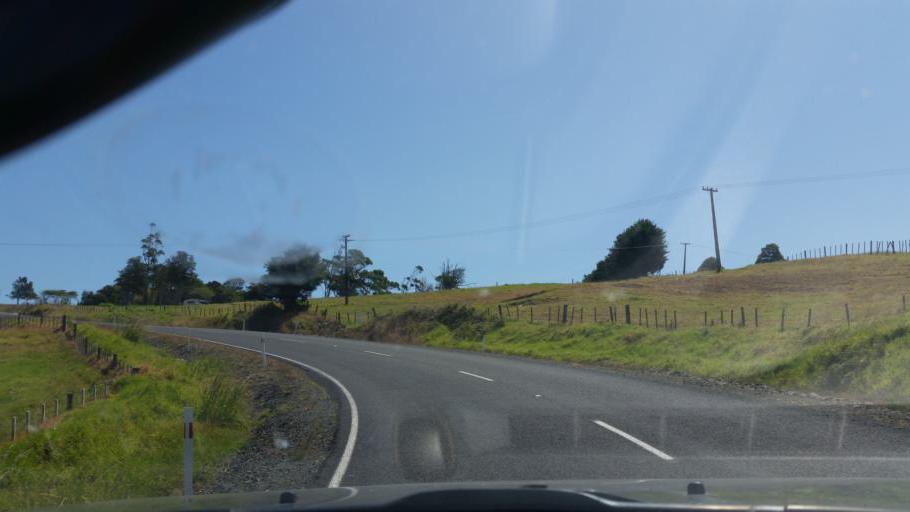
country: NZ
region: Northland
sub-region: Kaipara District
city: Dargaville
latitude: -36.0059
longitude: 173.9558
